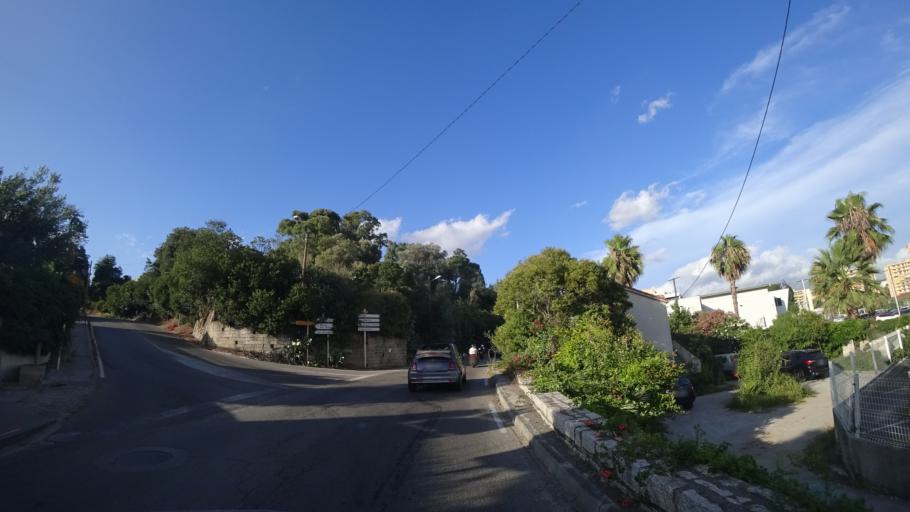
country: FR
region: Corsica
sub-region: Departement de la Corse-du-Sud
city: Ajaccio
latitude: 41.9373
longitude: 8.7360
